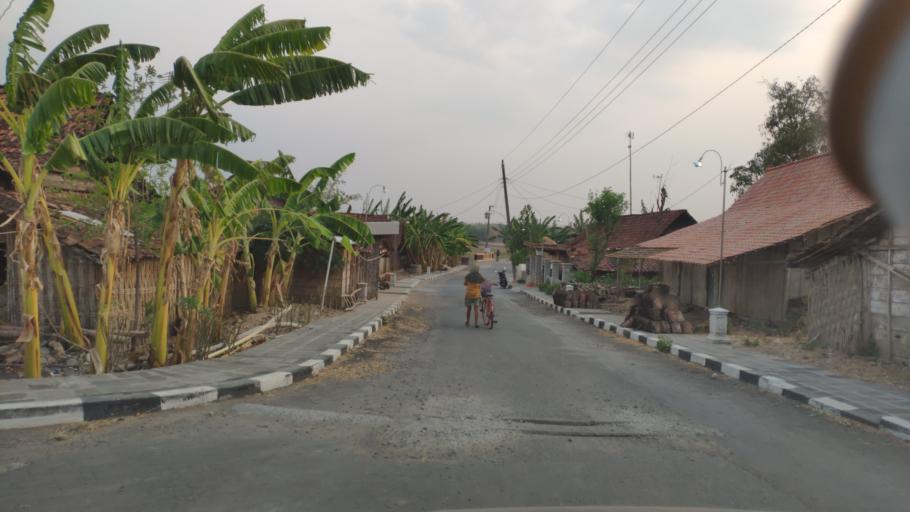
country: ID
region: Central Java
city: Kedungringin
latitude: -6.9887
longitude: 111.3549
